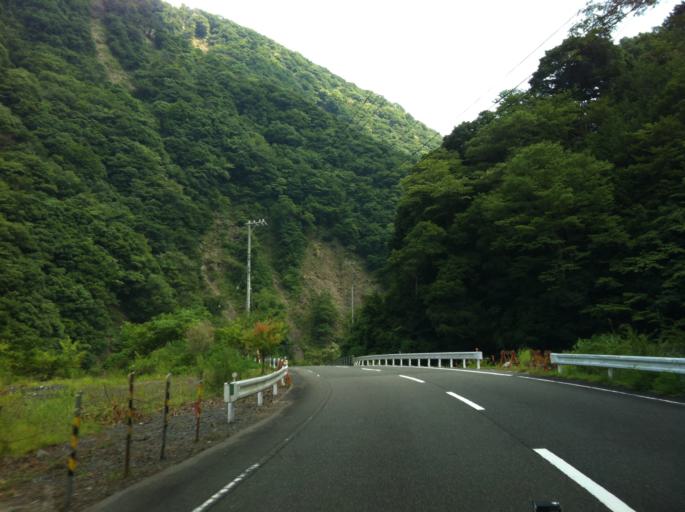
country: JP
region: Shizuoka
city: Shizuoka-shi
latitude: 35.2180
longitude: 138.3499
